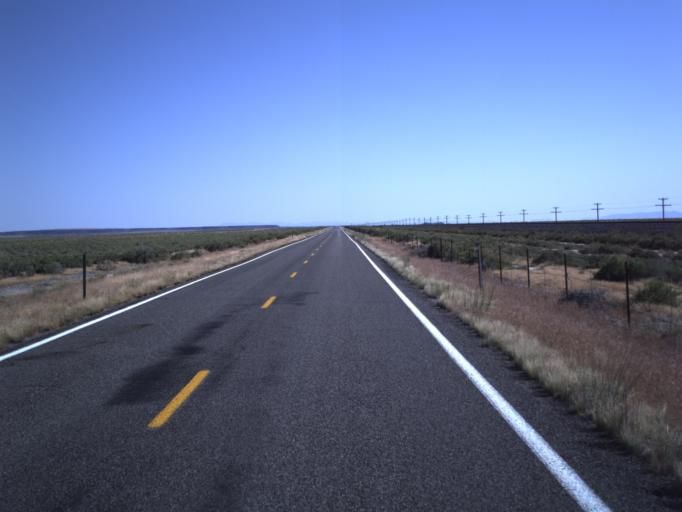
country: US
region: Utah
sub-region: Millard County
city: Delta
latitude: 39.0645
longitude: -112.7618
